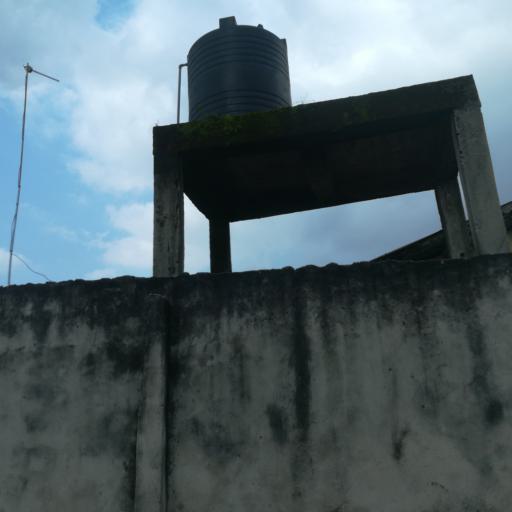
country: NG
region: Rivers
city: Okrika
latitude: 4.7981
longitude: 7.1233
